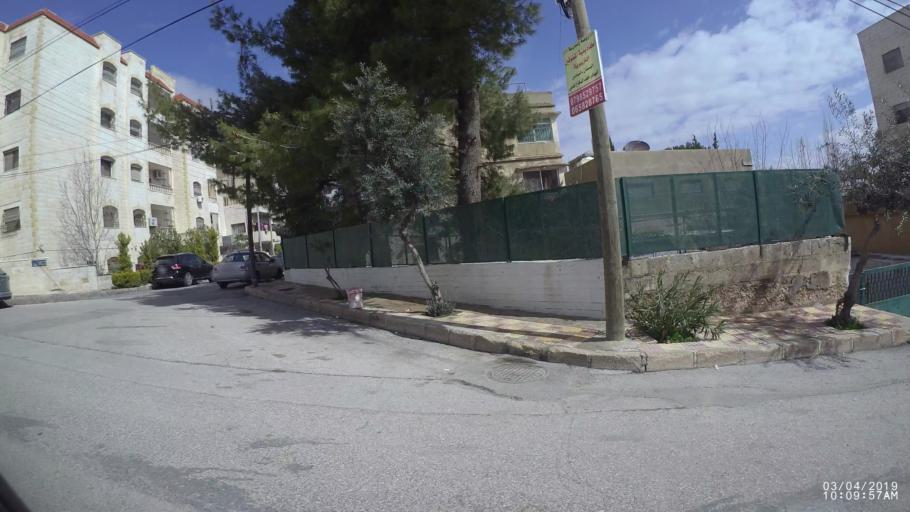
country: JO
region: Amman
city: Wadi as Sir
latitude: 31.9496
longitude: 35.8303
